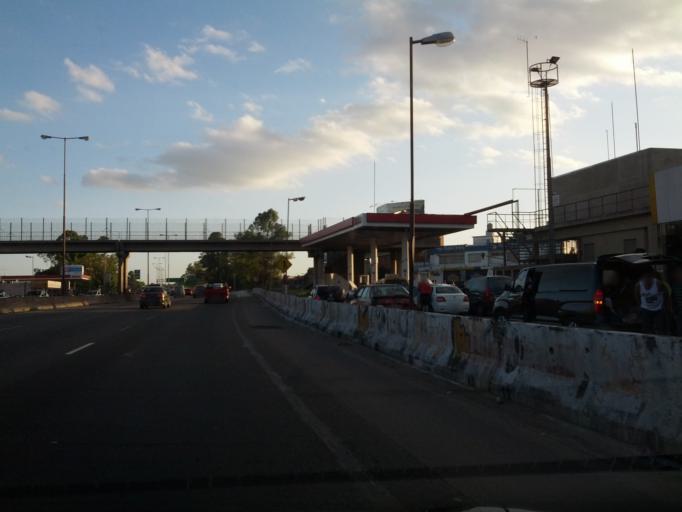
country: AR
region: Buenos Aires
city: San Justo
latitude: -34.6448
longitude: -58.5293
